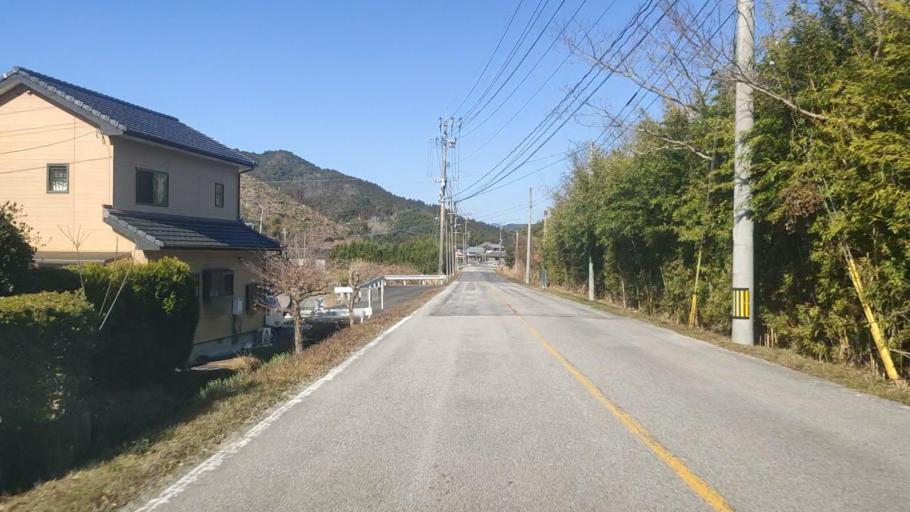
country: JP
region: Oita
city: Saiki
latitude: 32.9122
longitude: 131.9293
